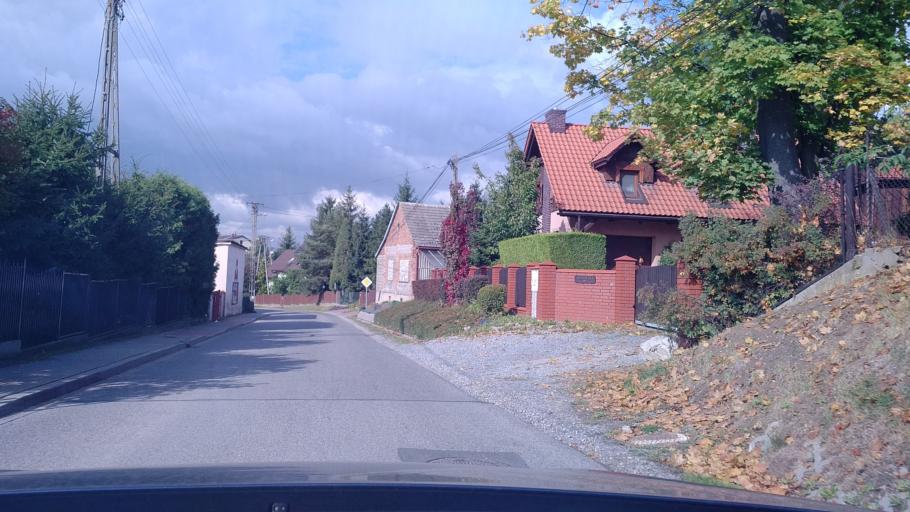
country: PL
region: Lesser Poland Voivodeship
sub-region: Powiat krakowski
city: Wielka Wies
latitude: 50.1346
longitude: 19.8401
